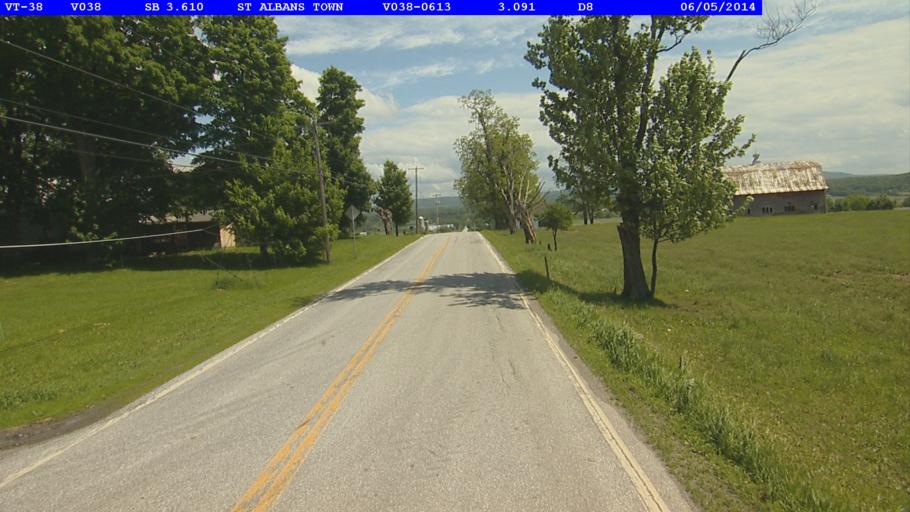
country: US
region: Vermont
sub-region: Franklin County
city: Swanton
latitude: 44.8537
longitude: -73.1328
